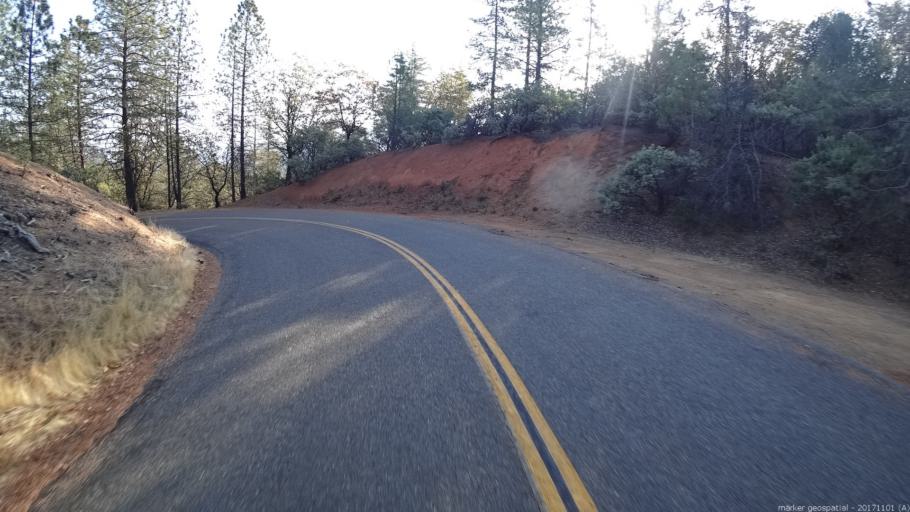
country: US
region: California
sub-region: Shasta County
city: Shasta Lake
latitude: 40.8039
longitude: -122.3081
